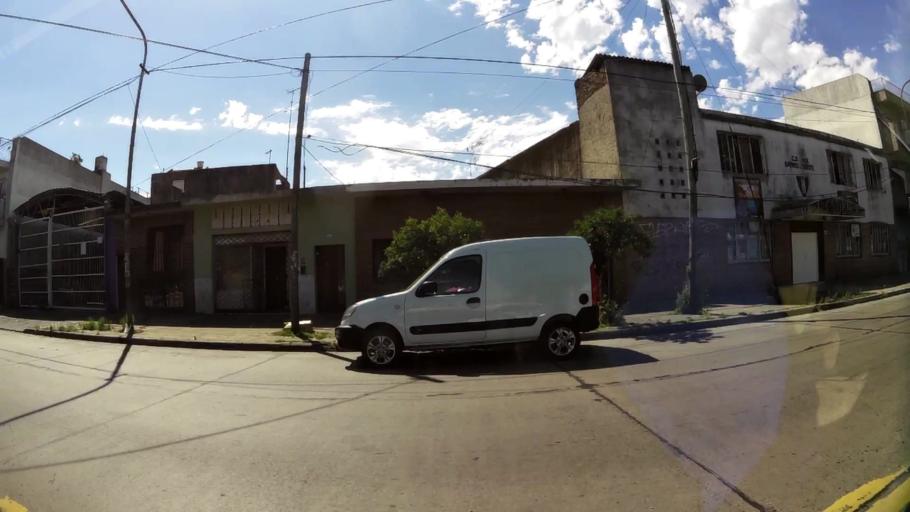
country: AR
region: Buenos Aires
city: San Justo
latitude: -34.6685
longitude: -58.5550
